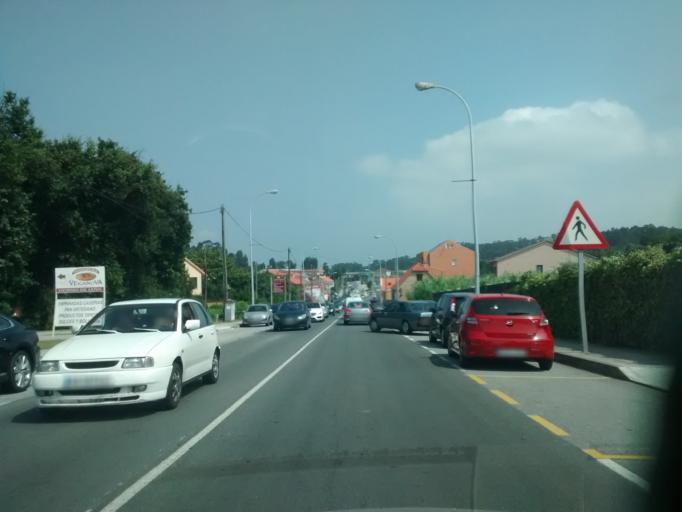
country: ES
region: Galicia
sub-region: Provincia de Pontevedra
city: Sanxenxo
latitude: 42.4091
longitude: -8.8129
